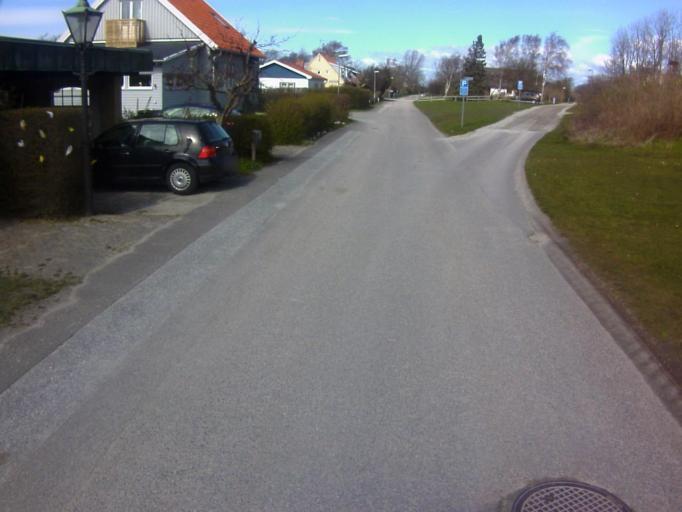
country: SE
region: Skane
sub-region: Kavlinge Kommun
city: Hofterup
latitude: 55.7573
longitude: 12.9073
